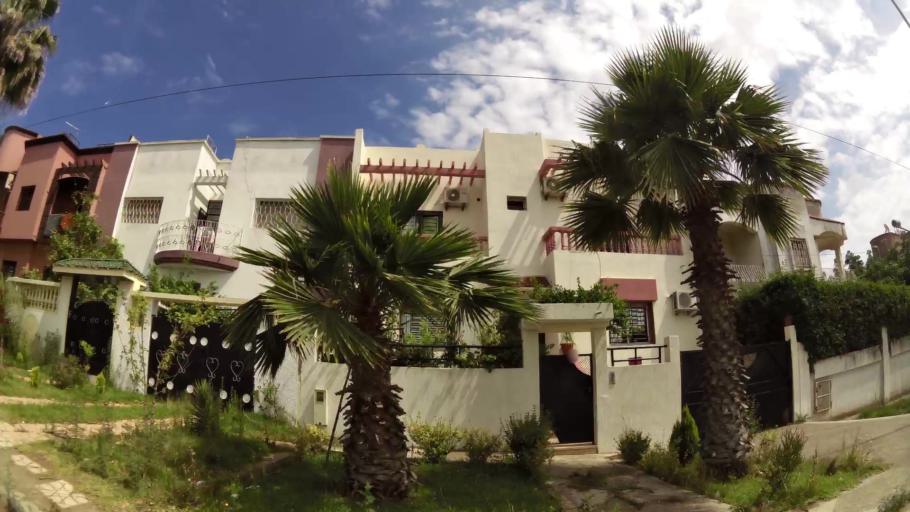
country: MA
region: Gharb-Chrarda-Beni Hssen
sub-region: Kenitra Province
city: Kenitra
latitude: 34.2414
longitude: -6.6045
